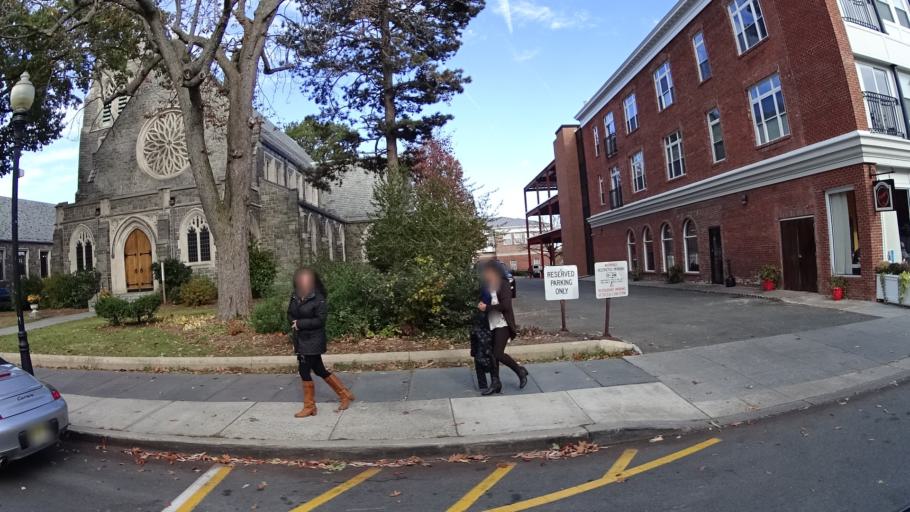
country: US
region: New Jersey
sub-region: Morris County
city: Morristown
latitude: 40.7952
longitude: -74.4797
